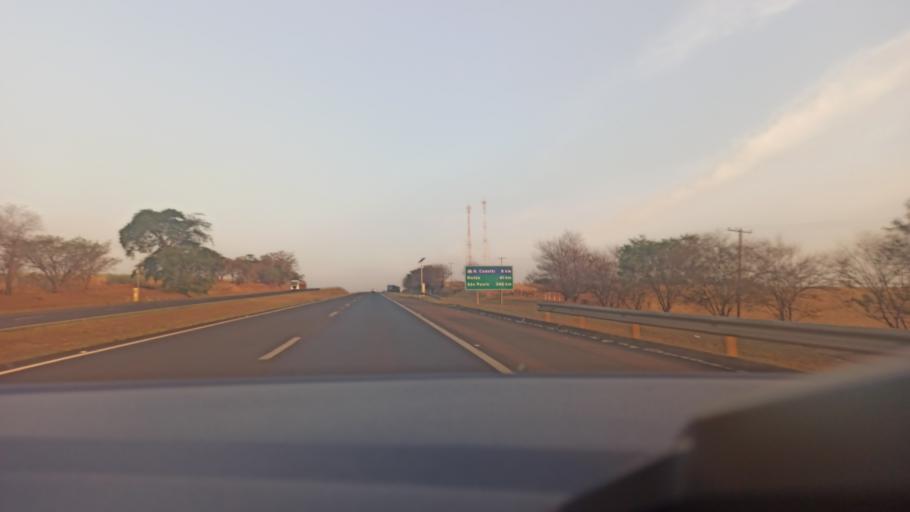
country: BR
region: Sao Paulo
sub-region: Taquaritinga
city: Taquaritinga
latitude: -21.4197
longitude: -48.6796
